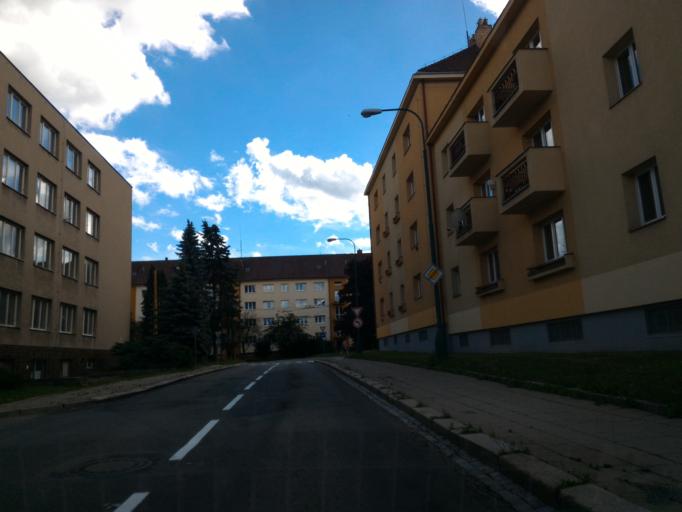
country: CZ
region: Vysocina
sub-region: Okres Jihlava
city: Jihlava
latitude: 49.3974
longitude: 15.5770
